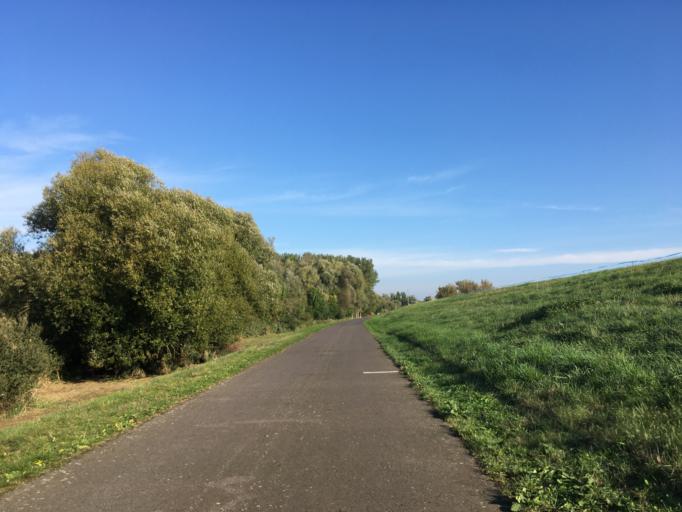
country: DE
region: Brandenburg
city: Reitwein
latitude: 52.5313
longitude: 14.6018
